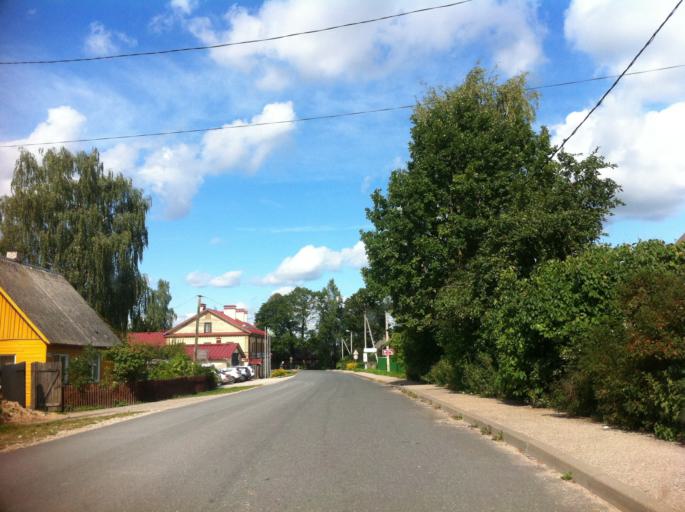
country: RU
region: Pskov
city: Izborsk
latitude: 57.7056
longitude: 27.8637
